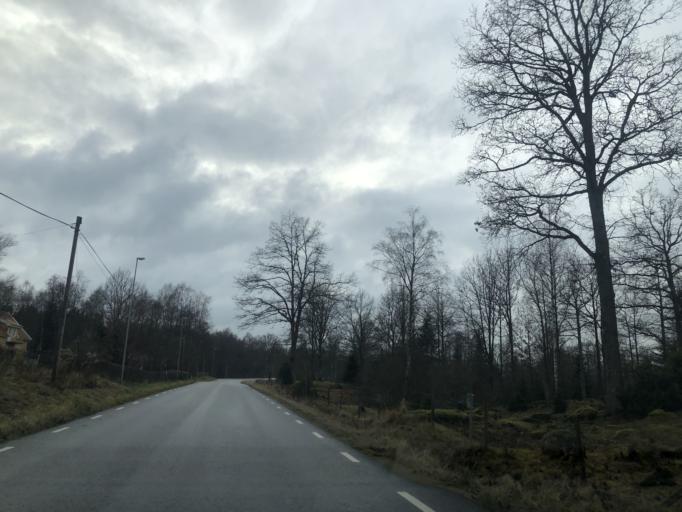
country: SE
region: Vaestra Goetaland
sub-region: Ulricehamns Kommun
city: Ulricehamn
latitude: 57.8319
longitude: 13.2588
